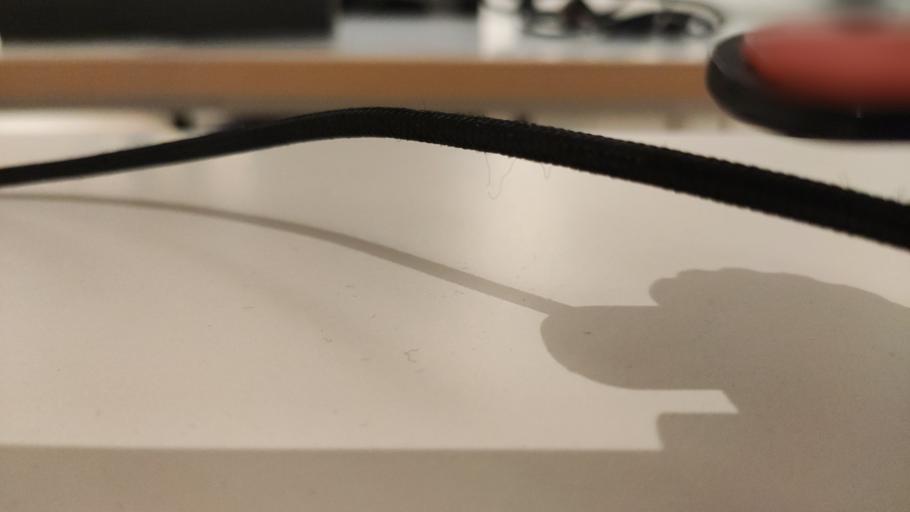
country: RU
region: Moskovskaya
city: Dorokhovo
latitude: 55.4933
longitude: 36.3515
